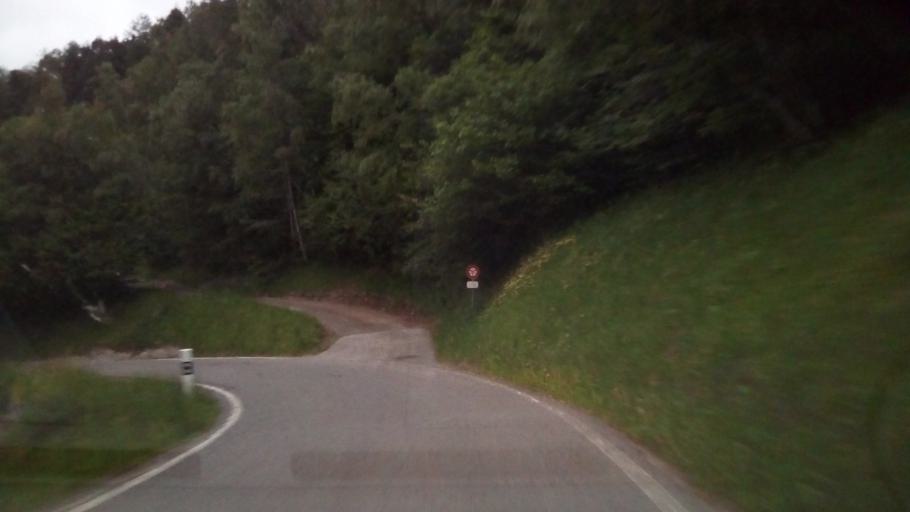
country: CH
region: Valais
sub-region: Entremont District
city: Orsieres
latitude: 46.0641
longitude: 7.1551
